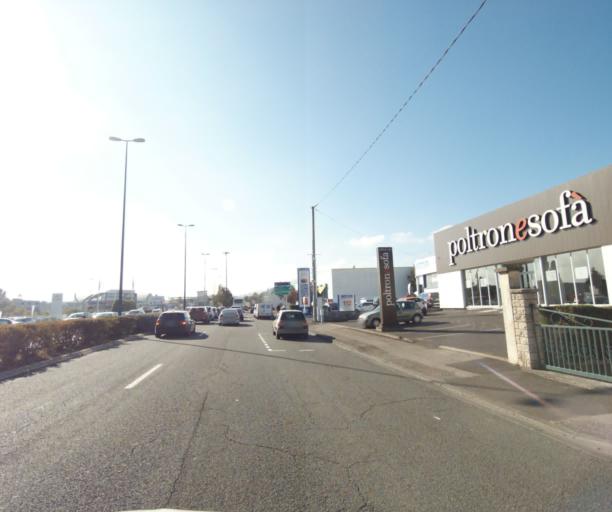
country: FR
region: Auvergne
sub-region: Departement du Puy-de-Dome
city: Aubiere
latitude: 45.7661
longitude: 3.1252
